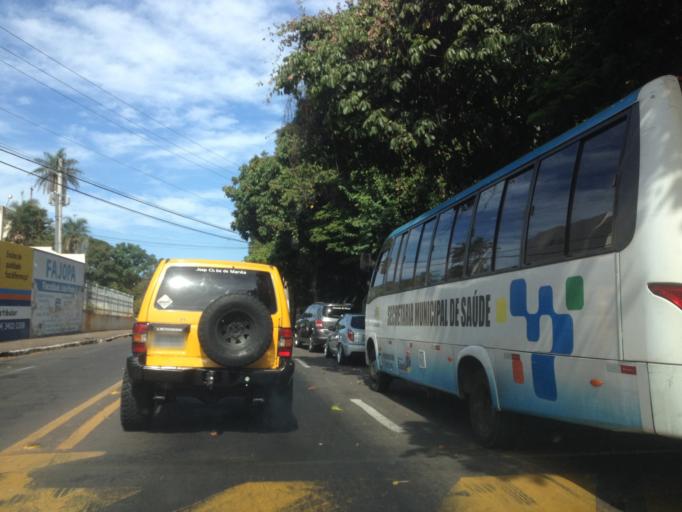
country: BR
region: Sao Paulo
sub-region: Marilia
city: Marilia
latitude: -22.2057
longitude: -49.9340
